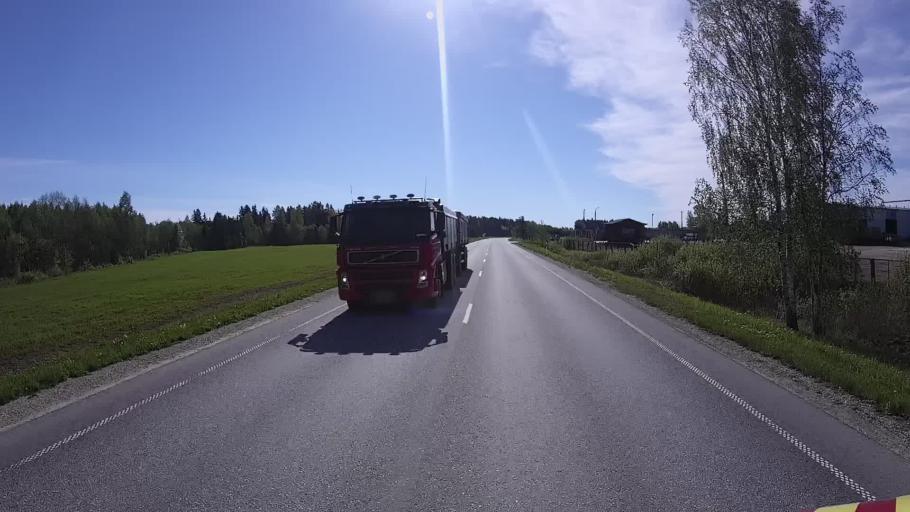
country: EE
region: Tartu
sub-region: Tartu linn
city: Tartu
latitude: 58.3514
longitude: 26.9250
